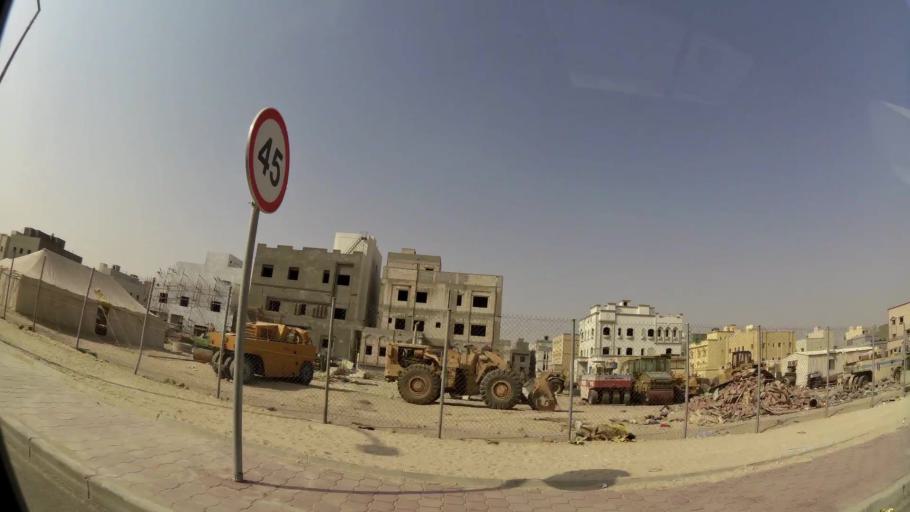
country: KW
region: Muhafazat al Jahra'
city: Al Jahra'
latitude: 29.3485
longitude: 47.7533
